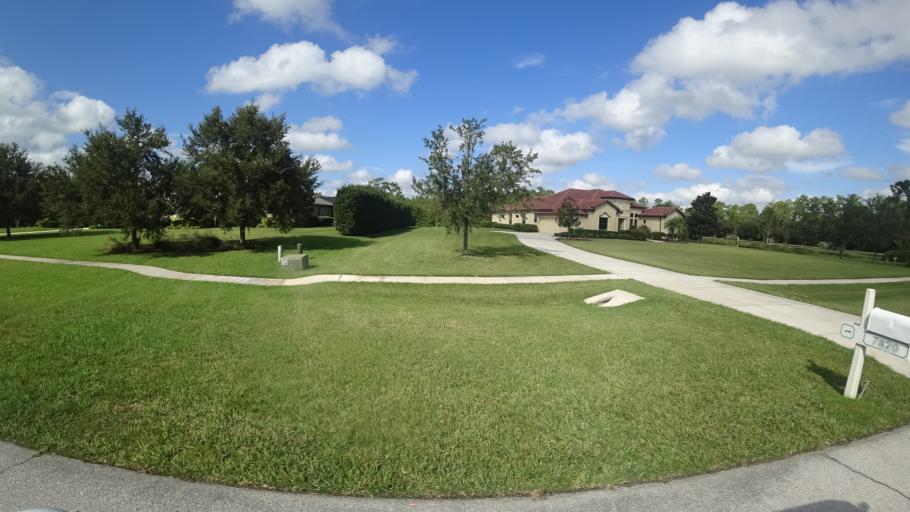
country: US
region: Florida
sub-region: Sarasota County
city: Fruitville
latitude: 27.3986
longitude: -82.3097
